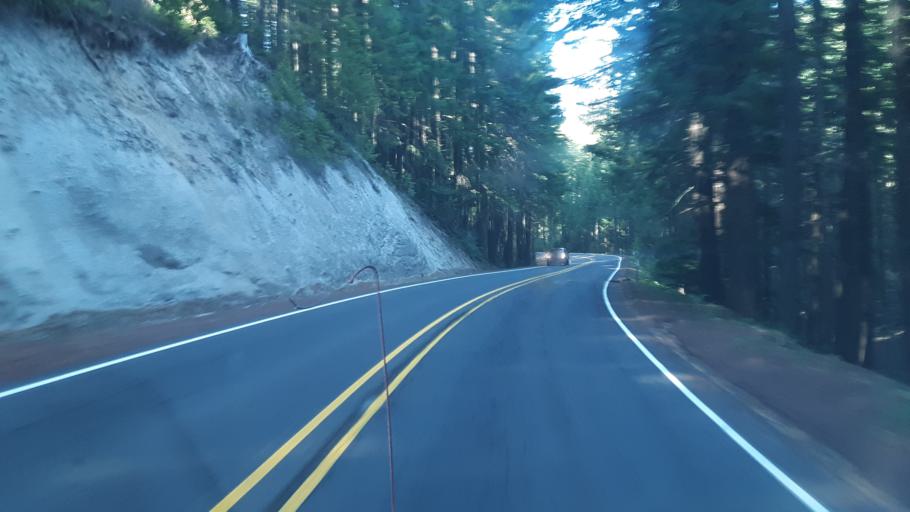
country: US
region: Oregon
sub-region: Jackson County
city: Shady Cove
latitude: 42.9366
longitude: -122.4203
